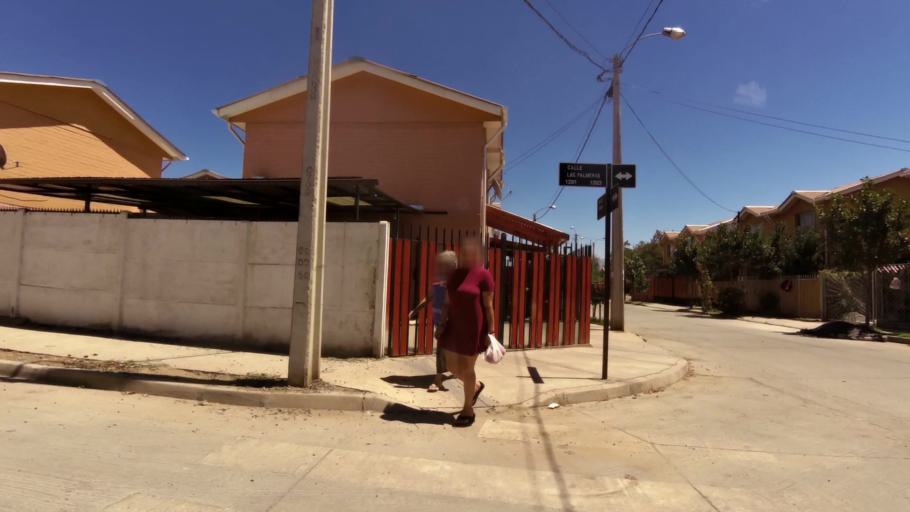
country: CL
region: O'Higgins
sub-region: Provincia de Cachapoal
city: Rancagua
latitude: -34.1521
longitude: -70.7094
